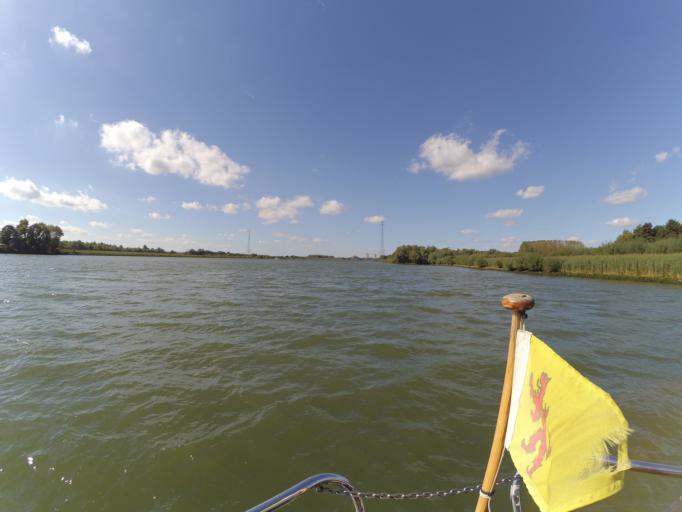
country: NL
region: South Holland
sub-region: Gemeente Oud-Beijerland
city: Oud-Beijerland
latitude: 51.8429
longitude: 4.3919
